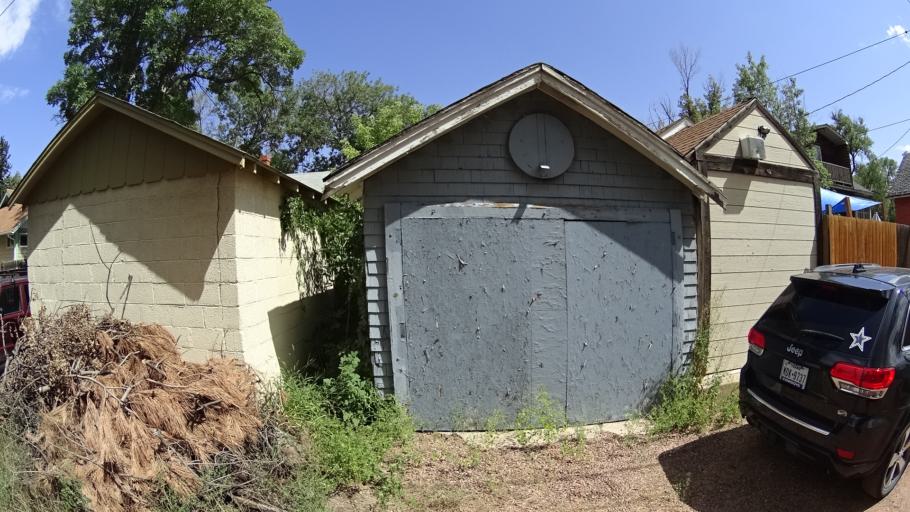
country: US
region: Colorado
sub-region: El Paso County
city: Colorado Springs
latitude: 38.8505
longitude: -104.8079
